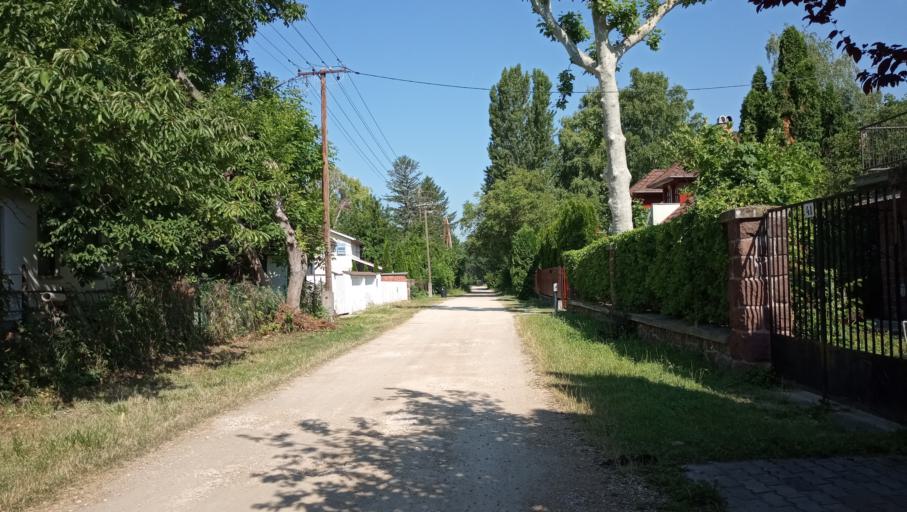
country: HU
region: Veszprem
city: Balatonkenese
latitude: 47.0367
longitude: 18.0882
